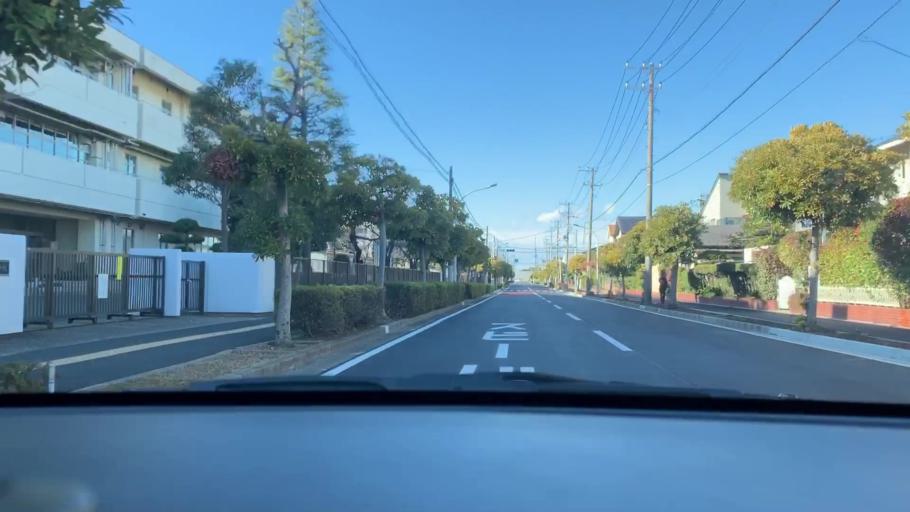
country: JP
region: Tokyo
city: Urayasu
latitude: 35.6383
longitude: 139.8974
